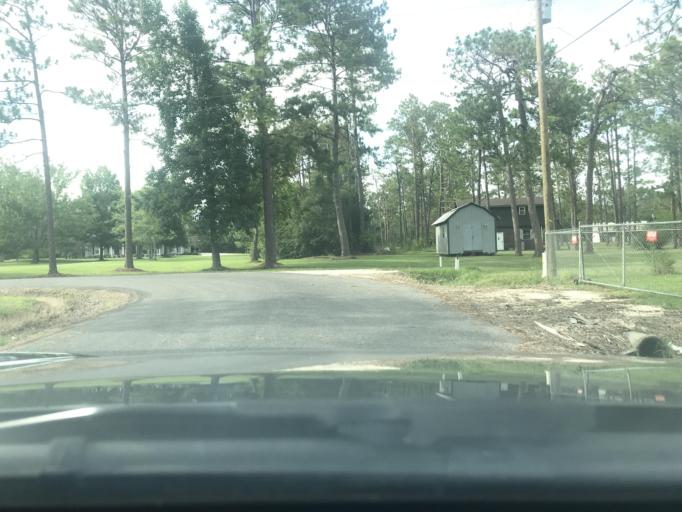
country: US
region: Louisiana
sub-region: Calcasieu Parish
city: Moss Bluff
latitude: 30.3388
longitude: -93.2625
